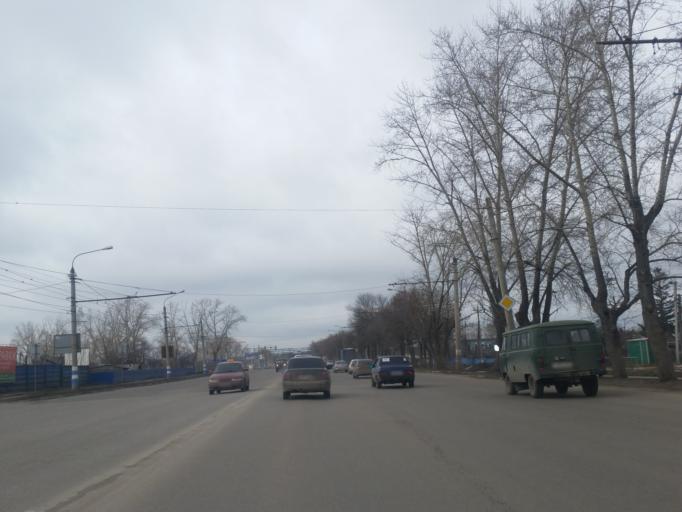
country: RU
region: Ulyanovsk
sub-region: Ulyanovskiy Rayon
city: Ulyanovsk
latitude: 54.3368
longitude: 48.5361
